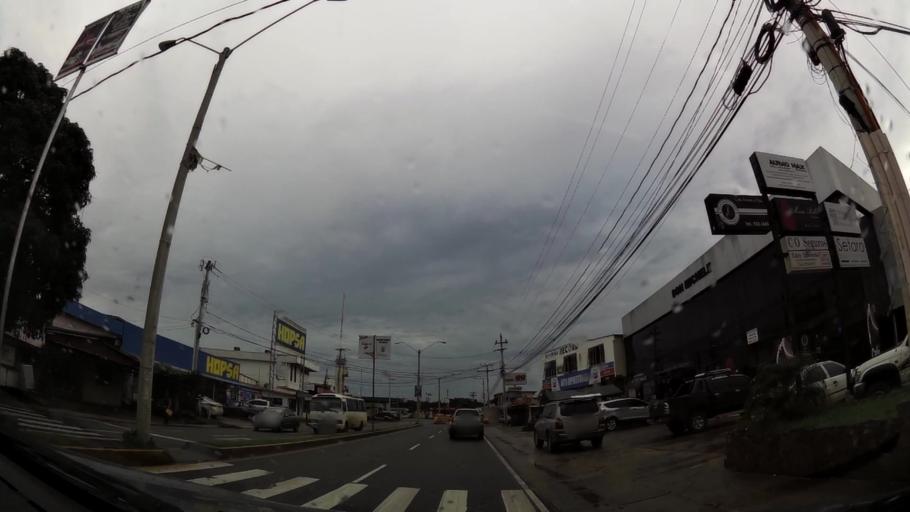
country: PA
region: Veraguas
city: Santiago de Veraguas
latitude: 8.0988
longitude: -80.9766
